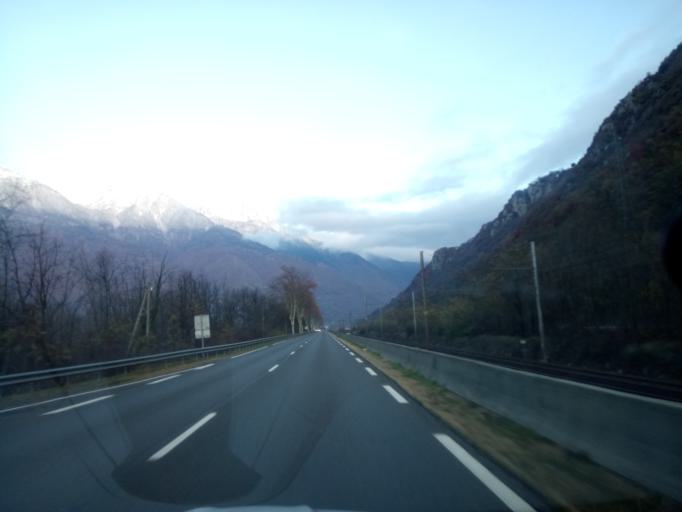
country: FR
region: Rhone-Alpes
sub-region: Departement de la Savoie
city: La Chambre
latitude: 45.3744
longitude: 6.2843
